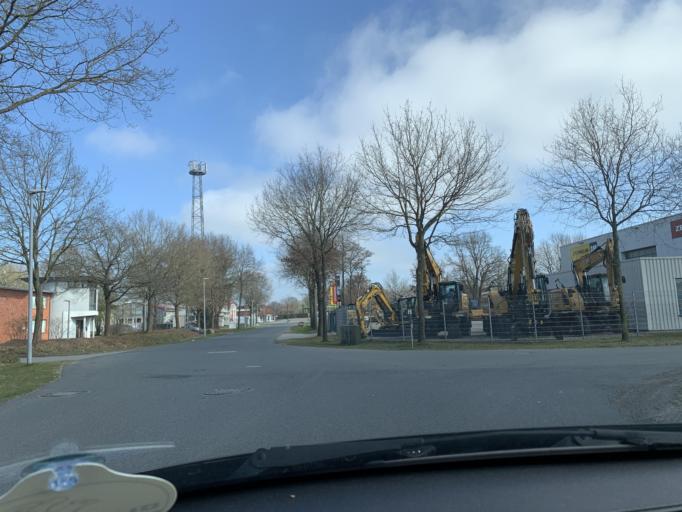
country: DE
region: Lower Saxony
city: Westerstede
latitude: 53.2861
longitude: 7.8911
